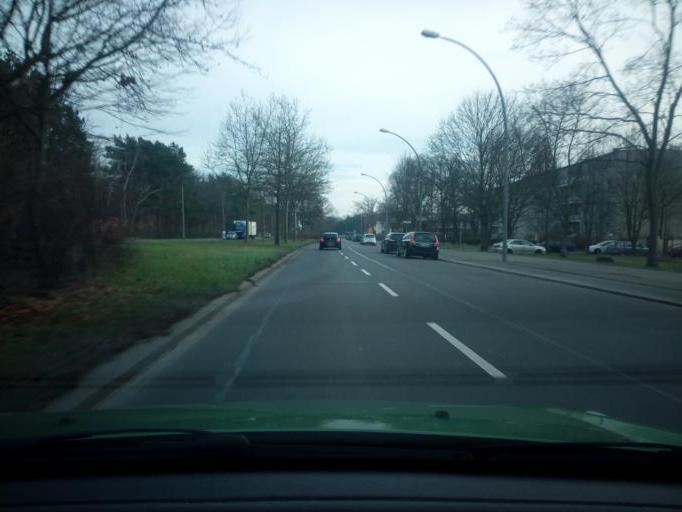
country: DE
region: Berlin
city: Oberschoneweide
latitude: 52.4610
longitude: 13.5340
